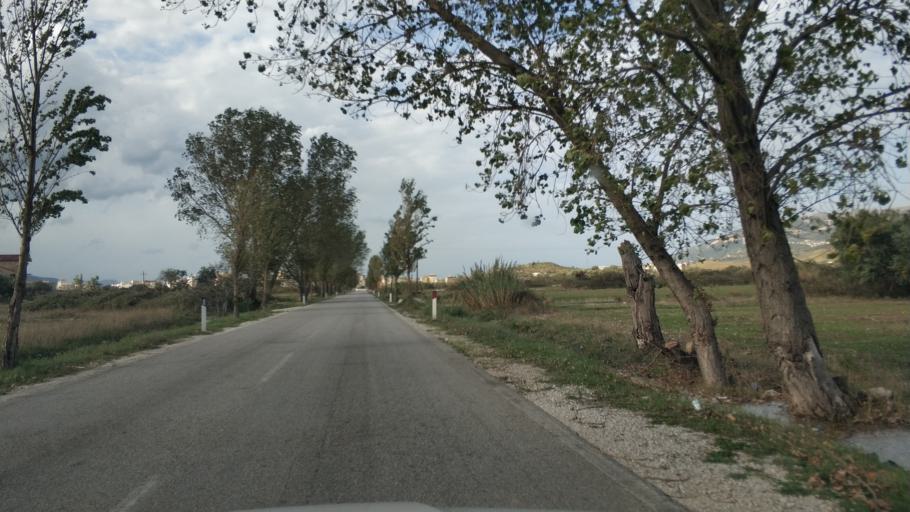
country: AL
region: Vlore
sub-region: Rrethi i Vlores
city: Orikum
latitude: 40.3209
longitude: 19.4819
